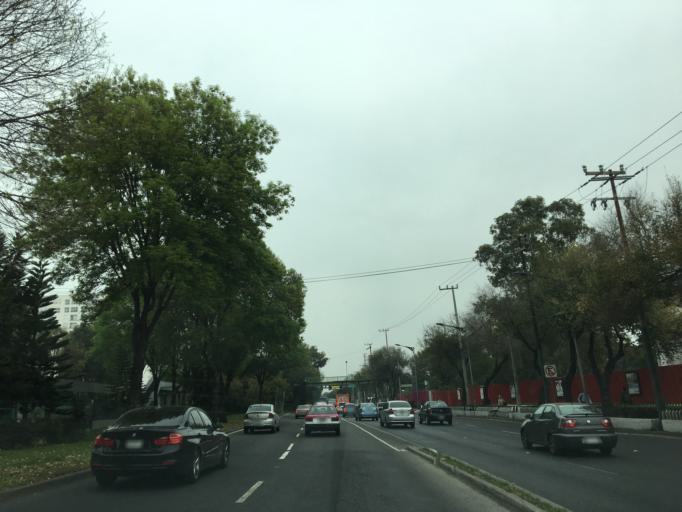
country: MX
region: Mexico City
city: Tlalpan
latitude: 19.3122
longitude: -99.1404
